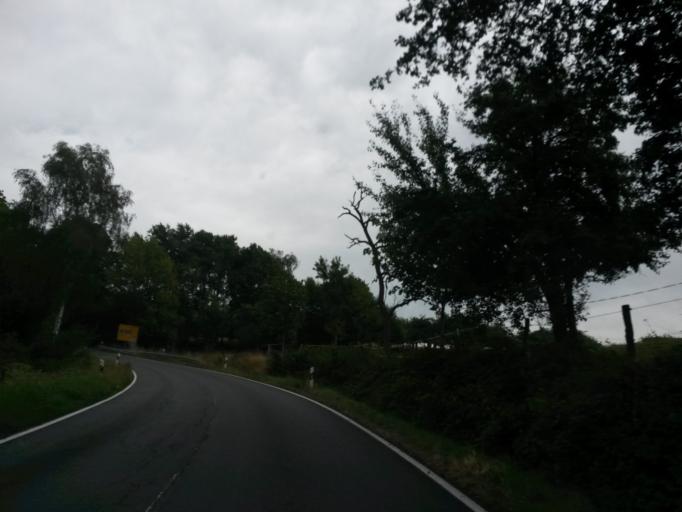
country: DE
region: North Rhine-Westphalia
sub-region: Regierungsbezirk Koln
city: Numbrecht
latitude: 50.8887
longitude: 7.5348
